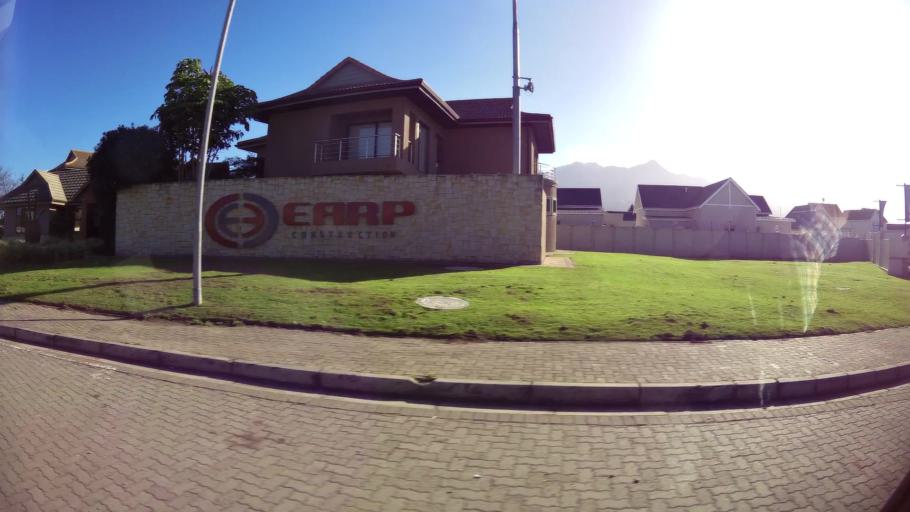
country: ZA
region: Western Cape
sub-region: Eden District Municipality
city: George
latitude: -33.9642
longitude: 22.4295
